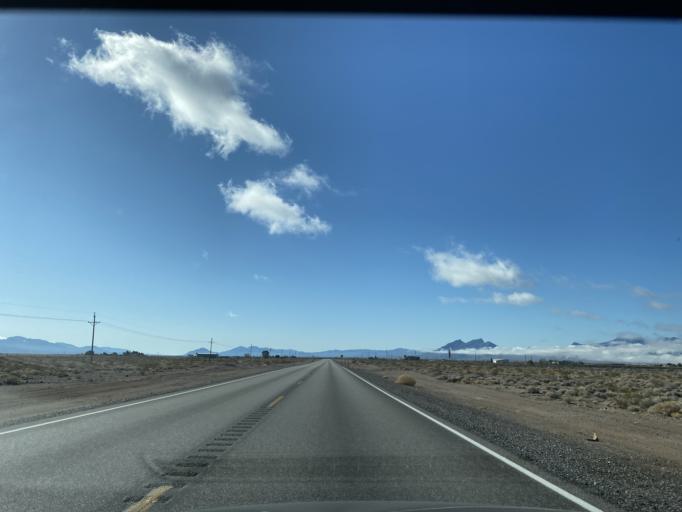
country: US
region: Nevada
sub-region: Nye County
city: Beatty
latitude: 36.5342
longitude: -116.4183
